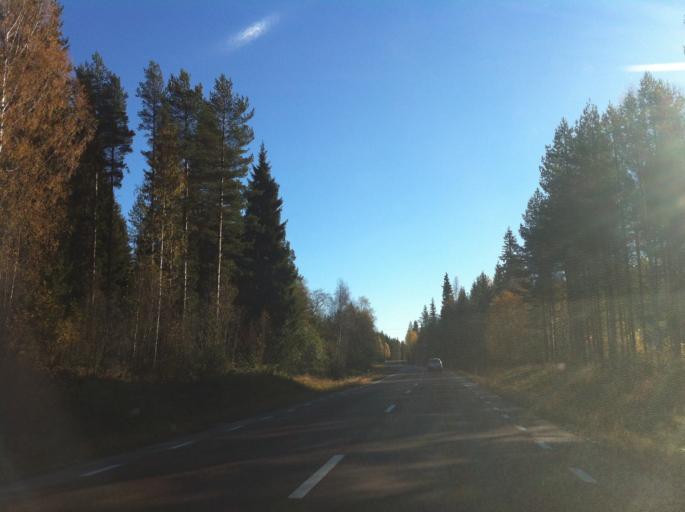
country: SE
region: Dalarna
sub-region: Alvdalens Kommun
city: AElvdalen
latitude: 61.1753
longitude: 14.1011
